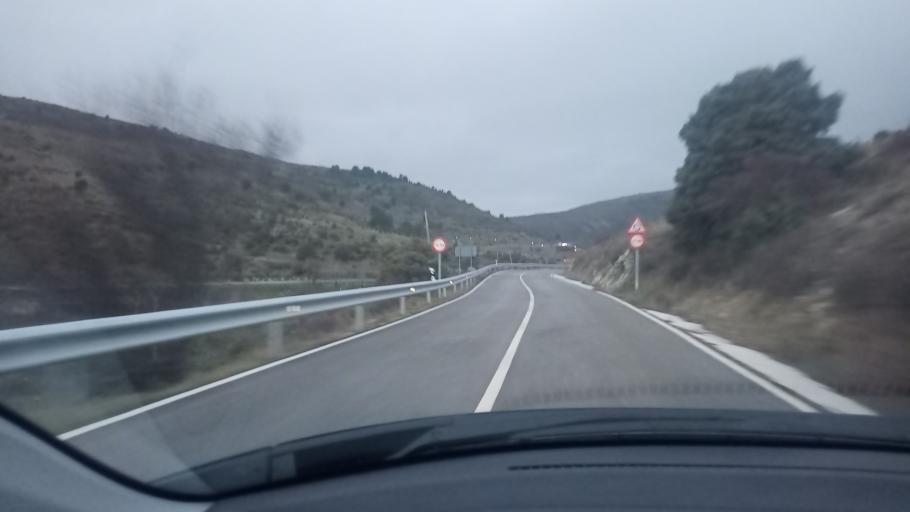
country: ES
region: Madrid
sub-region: Provincia de Madrid
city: Zarzalejo
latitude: 40.5562
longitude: -4.1963
